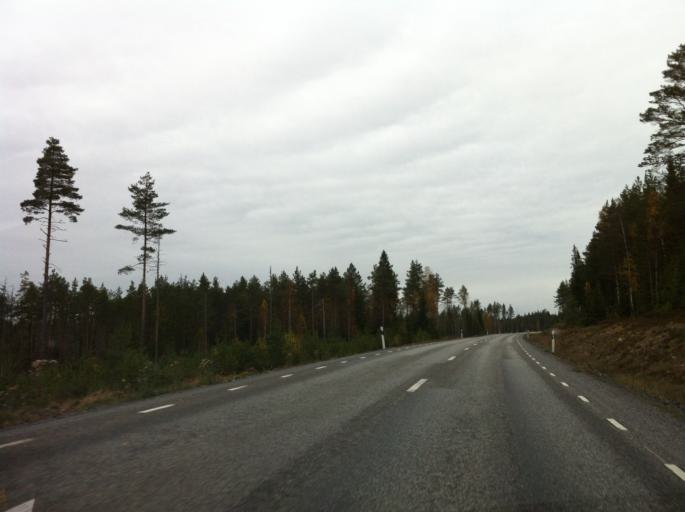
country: SE
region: OErebro
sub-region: Ljusnarsbergs Kommun
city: Kopparberg
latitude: 59.9468
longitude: 15.0220
